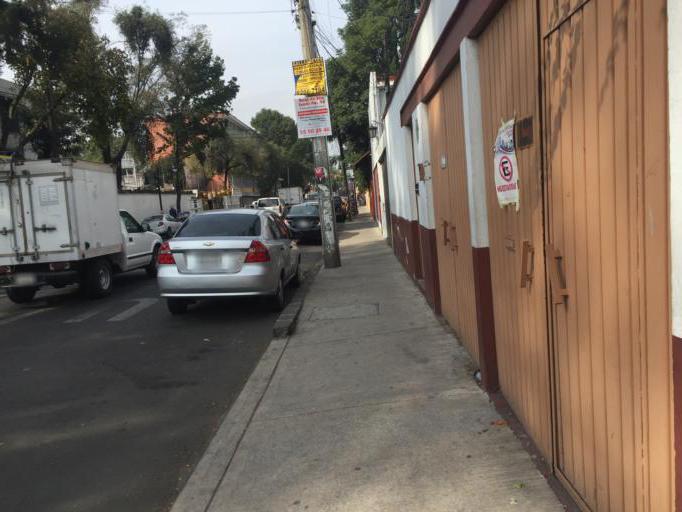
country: MX
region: Mexico City
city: Coyoacan
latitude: 19.3506
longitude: -99.1562
